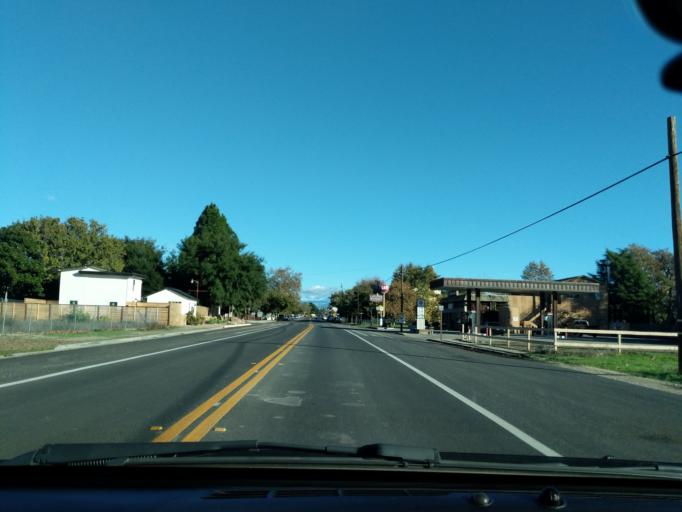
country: US
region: California
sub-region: Santa Barbara County
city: Los Alamos
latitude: 34.7442
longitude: -120.2825
